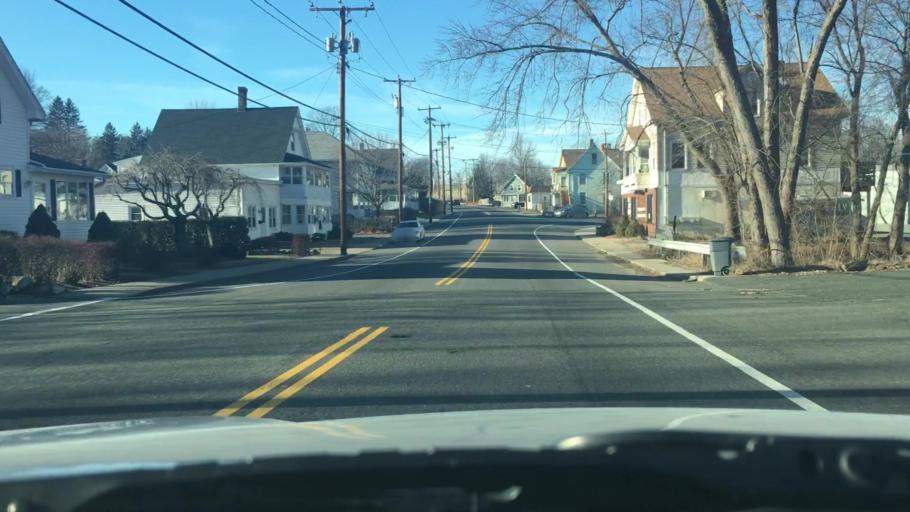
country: US
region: Massachusetts
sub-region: Hampden County
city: Ludlow
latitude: 42.1647
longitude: -72.4851
